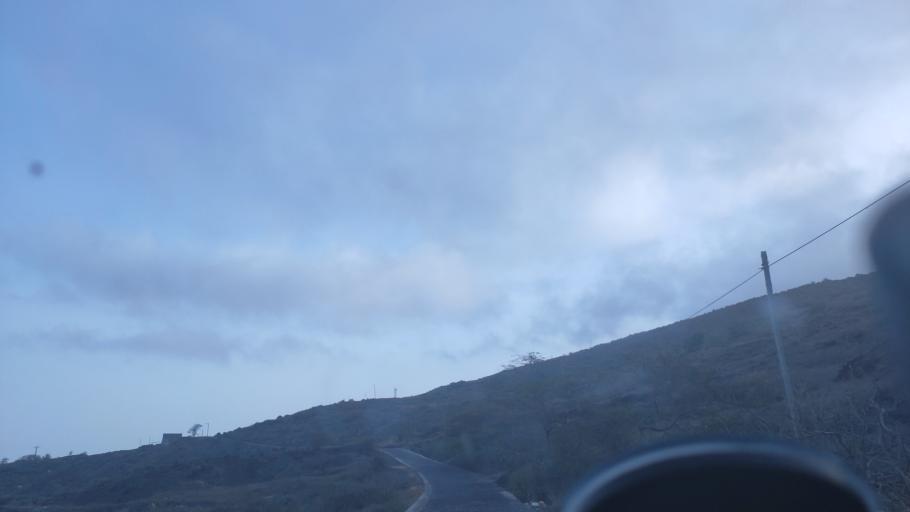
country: CV
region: Mosteiros
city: Porto dos Mosteiros
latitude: 15.0084
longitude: -24.3058
